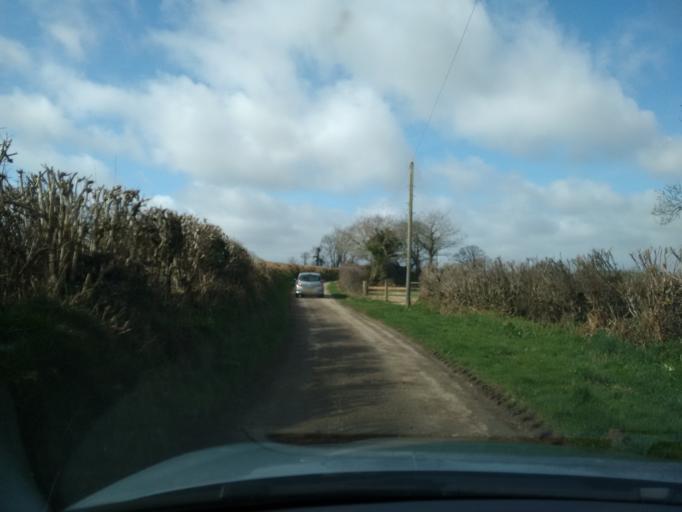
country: GB
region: England
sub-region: Cornwall
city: Launceston
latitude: 50.5968
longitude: -4.3534
